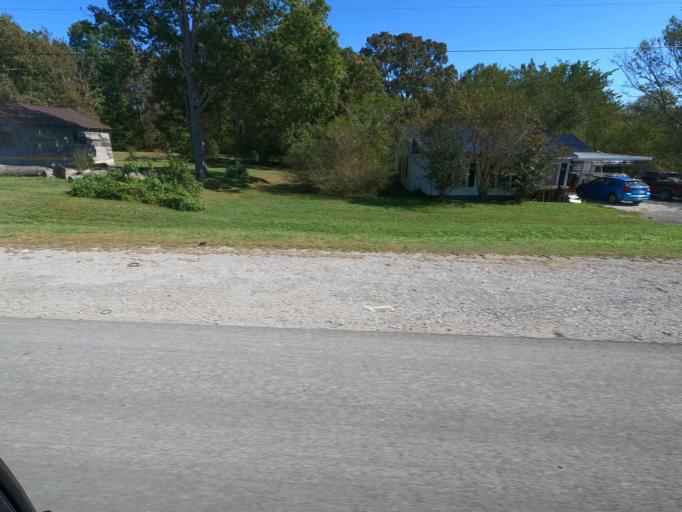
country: US
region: Tennessee
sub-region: Maury County
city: Mount Pleasant
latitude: 35.4293
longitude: -87.2812
